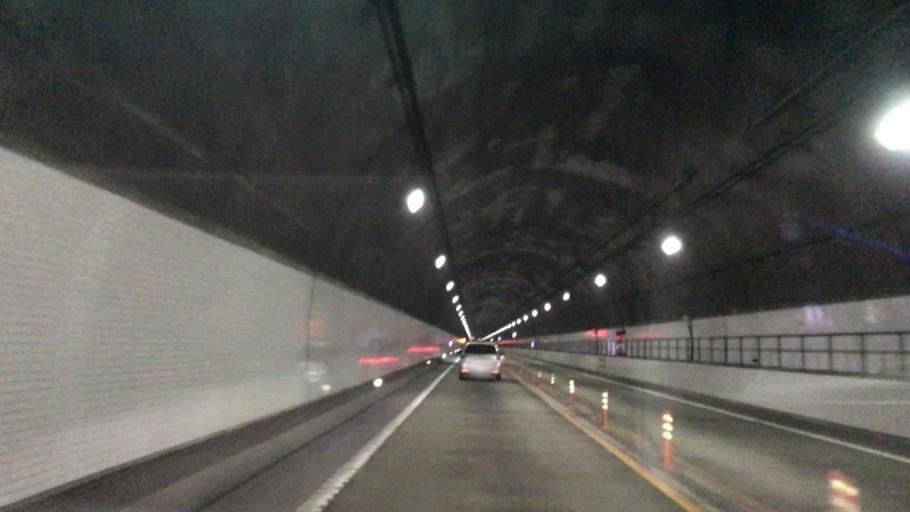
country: JP
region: Hokkaido
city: Shimo-furano
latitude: 42.9628
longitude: 142.3555
